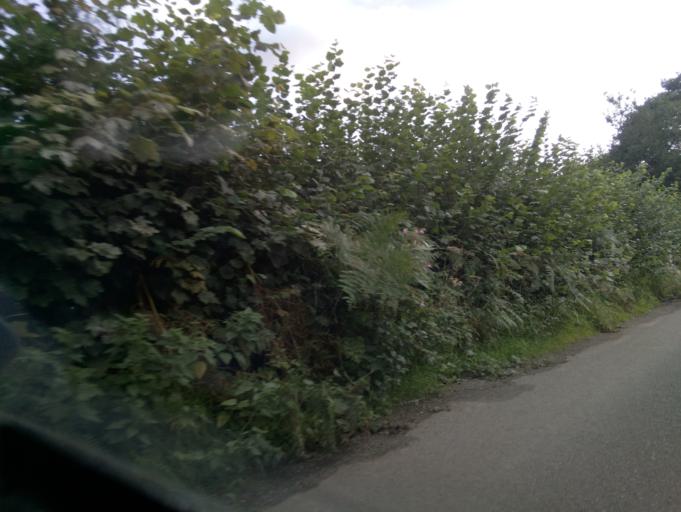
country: GB
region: Wales
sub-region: Cardiff
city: Pentyrch
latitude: 51.5554
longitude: -3.2762
